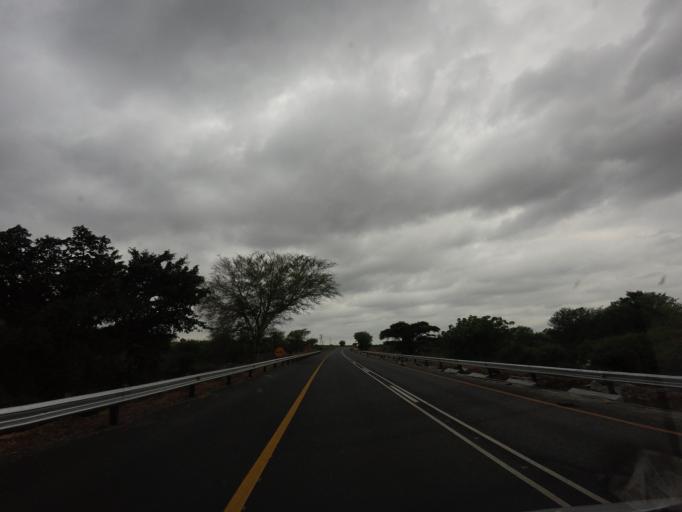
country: ZA
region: Mpumalanga
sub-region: Ehlanzeni District
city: Komatipoort
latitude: -25.4355
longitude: 31.8190
